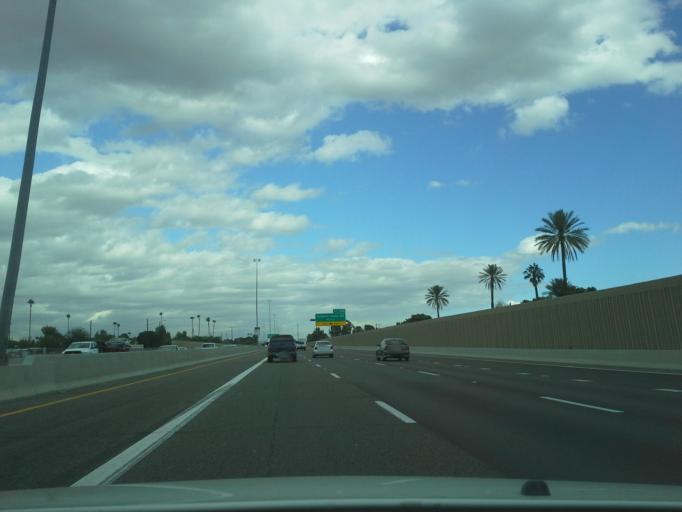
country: US
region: Arizona
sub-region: Maricopa County
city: Phoenix
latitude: 33.5133
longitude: -112.1123
